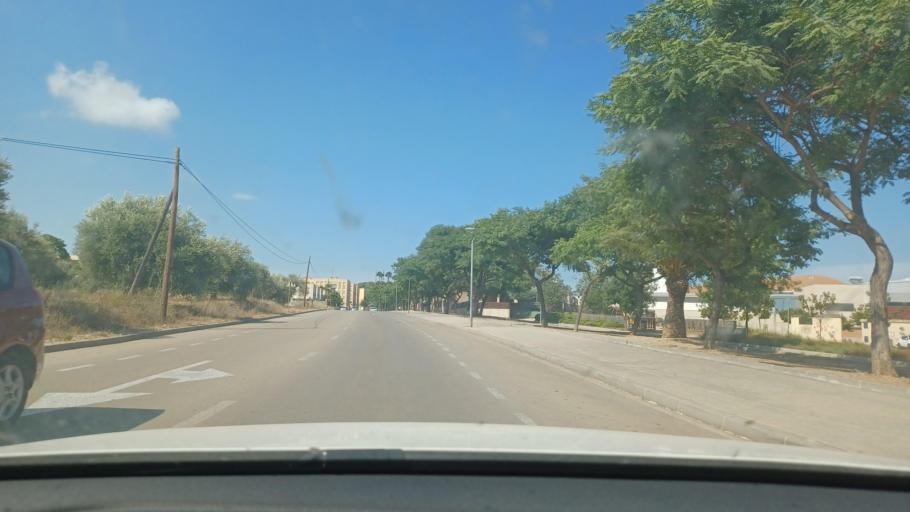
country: ES
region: Catalonia
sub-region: Provincia de Tarragona
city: Sant Carles de la Rapita
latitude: 40.6117
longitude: 0.5828
